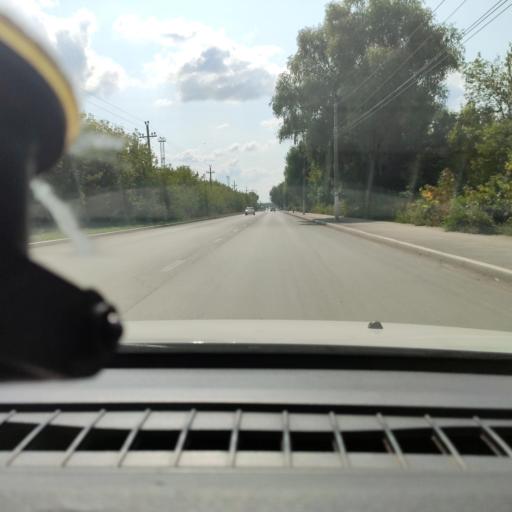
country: RU
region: Samara
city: Chapayevsk
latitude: 52.9823
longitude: 49.7064
